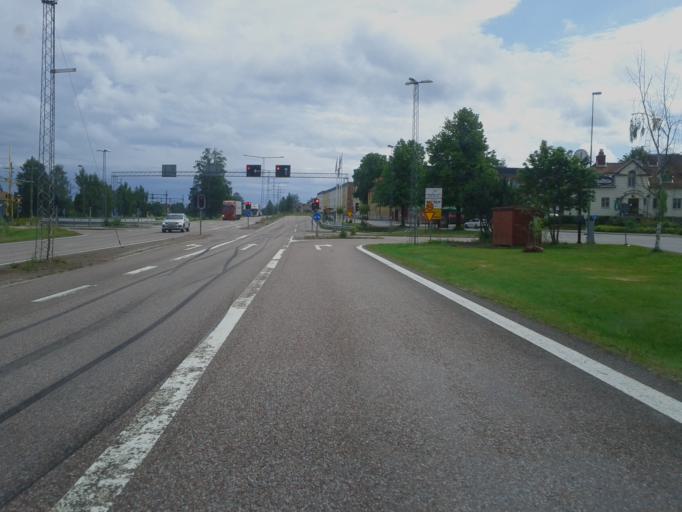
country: SE
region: Dalarna
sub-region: Saters Kommun
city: Saeter
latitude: 60.3477
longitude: 15.7511
